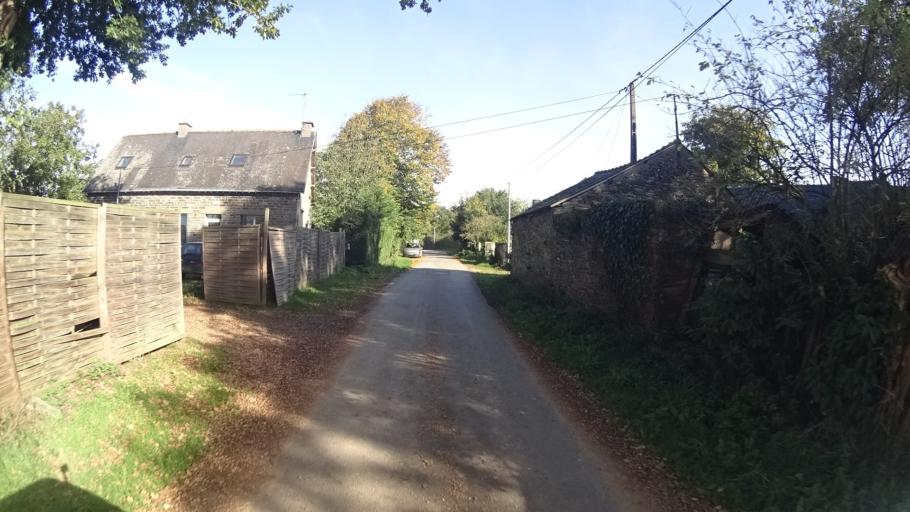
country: FR
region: Brittany
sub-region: Departement du Morbihan
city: Peillac
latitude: 47.7437
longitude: -2.2170
